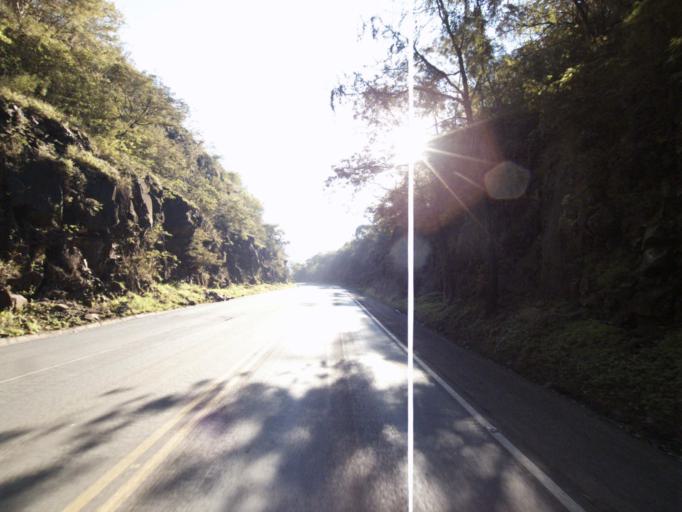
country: BR
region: Santa Catarina
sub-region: Chapeco
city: Chapeco
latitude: -26.9263
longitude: -52.8486
